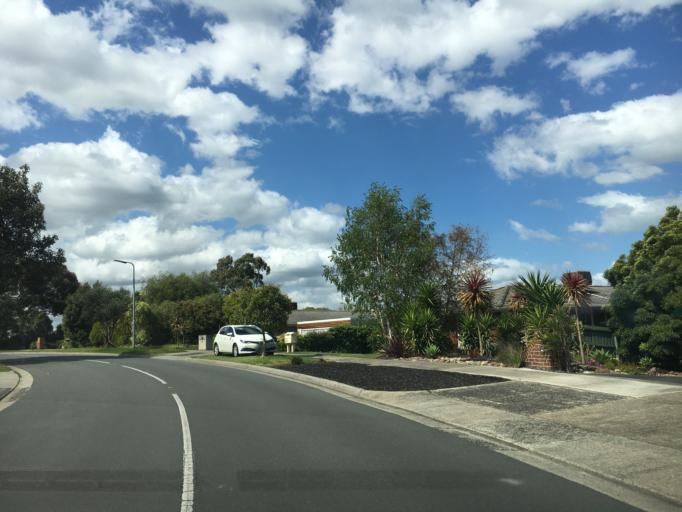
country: AU
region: Victoria
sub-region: Whitehorse
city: Vermont South
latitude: -37.8857
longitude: 145.1843
